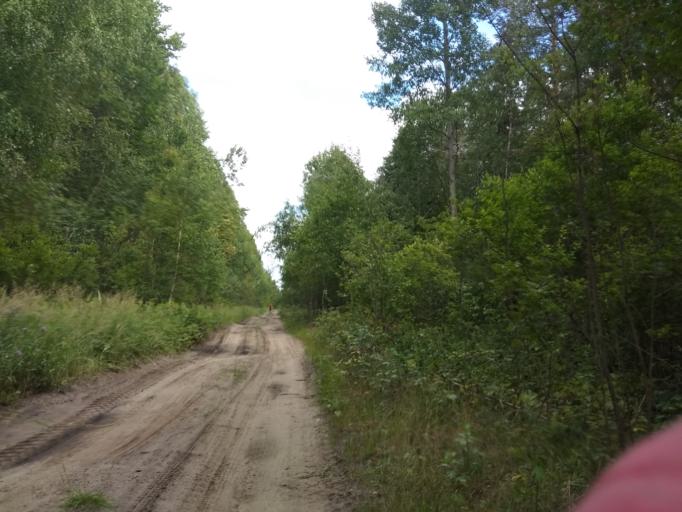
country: RU
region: Moskovskaya
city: Misheronskiy
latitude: 55.7091
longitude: 39.7290
